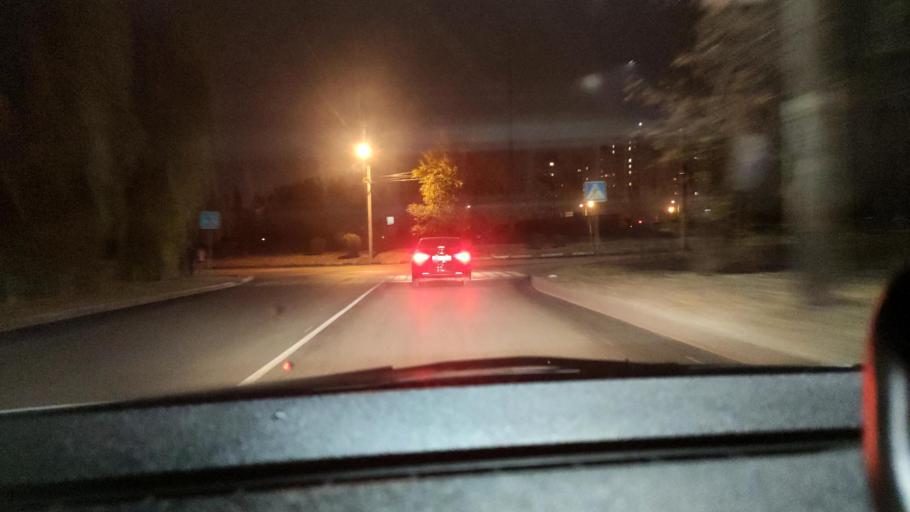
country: RU
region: Voronezj
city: Voronezh
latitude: 51.6583
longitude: 39.1309
